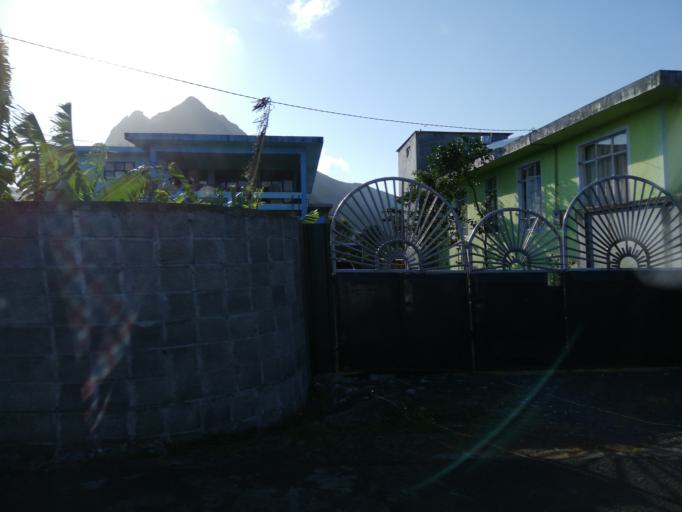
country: MU
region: Moka
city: Saint Pierre
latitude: -20.2151
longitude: 57.5247
